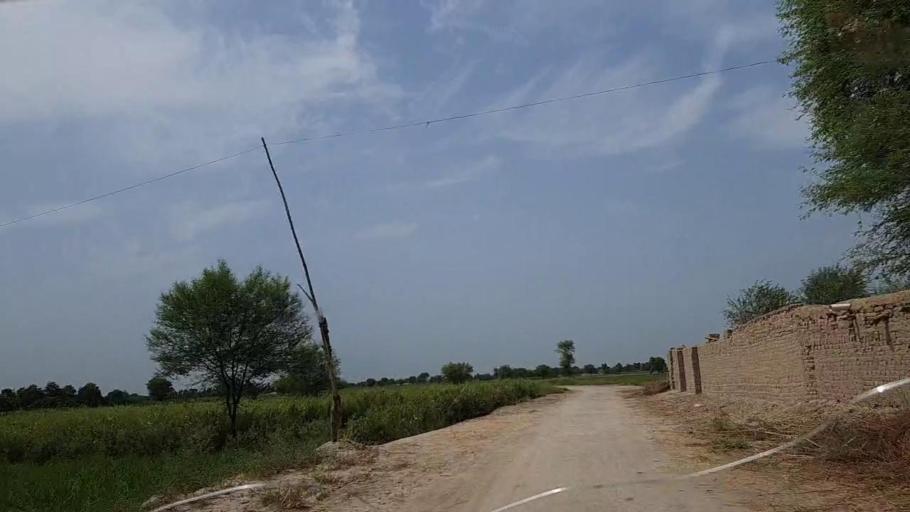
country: PK
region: Sindh
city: Tharu Shah
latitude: 26.8962
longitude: 68.0778
